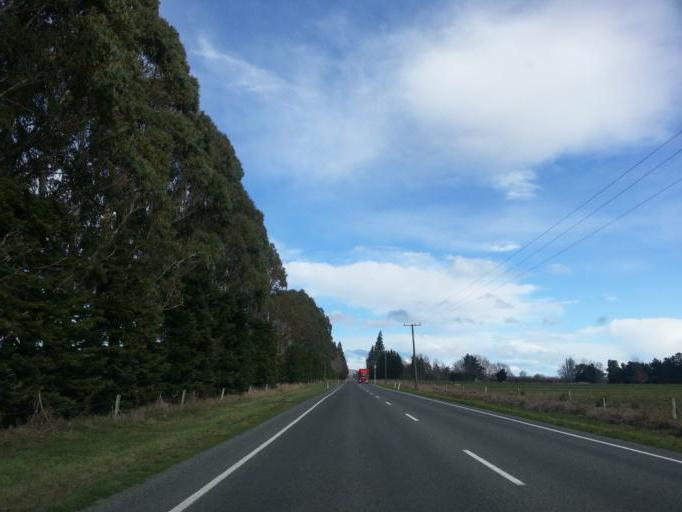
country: NZ
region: Canterbury
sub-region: Hurunui District
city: Amberley
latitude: -42.7885
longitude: 172.8366
